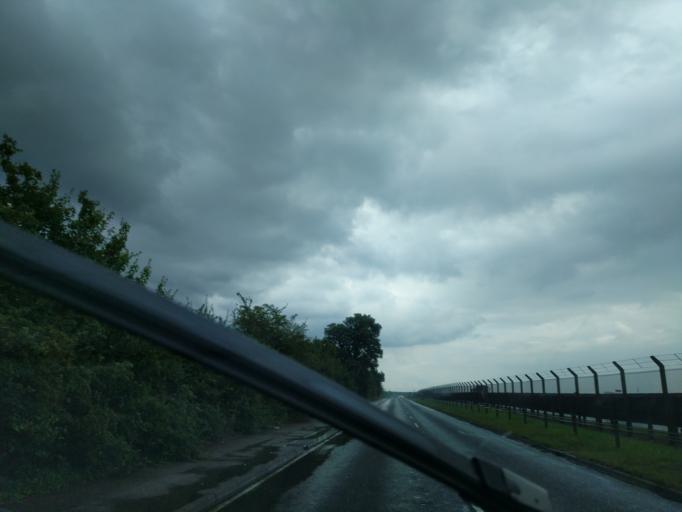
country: GB
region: England
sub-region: Suffolk
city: Lakenheath
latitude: 52.3644
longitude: 0.4946
